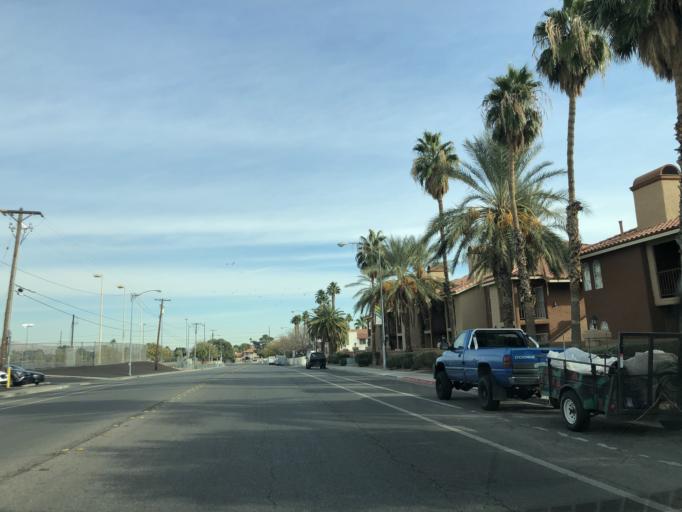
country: US
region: Nevada
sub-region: Clark County
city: Winchester
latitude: 36.1202
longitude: -115.1317
